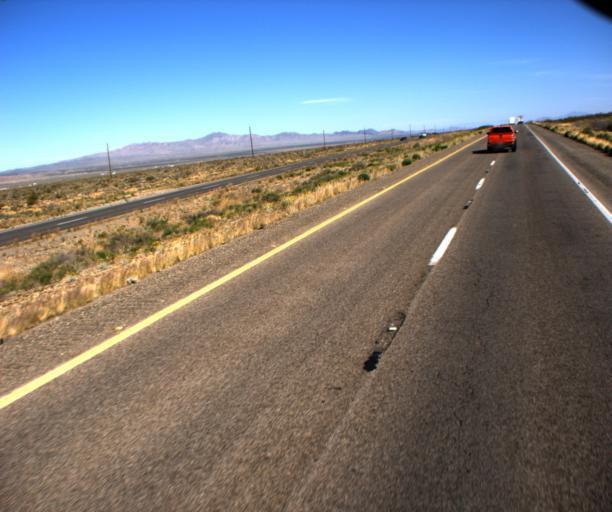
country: US
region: Arizona
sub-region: Mohave County
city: Dolan Springs
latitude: 35.4631
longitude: -114.3062
